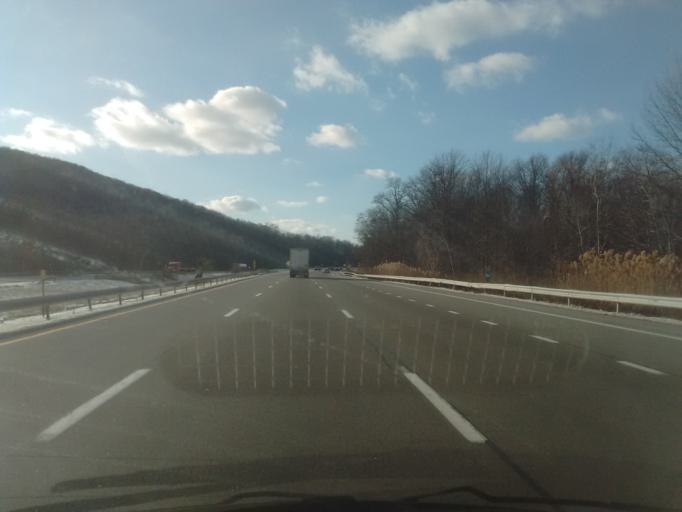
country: US
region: New York
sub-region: Dutchess County
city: Fishkill
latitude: 41.5229
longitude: -73.8993
